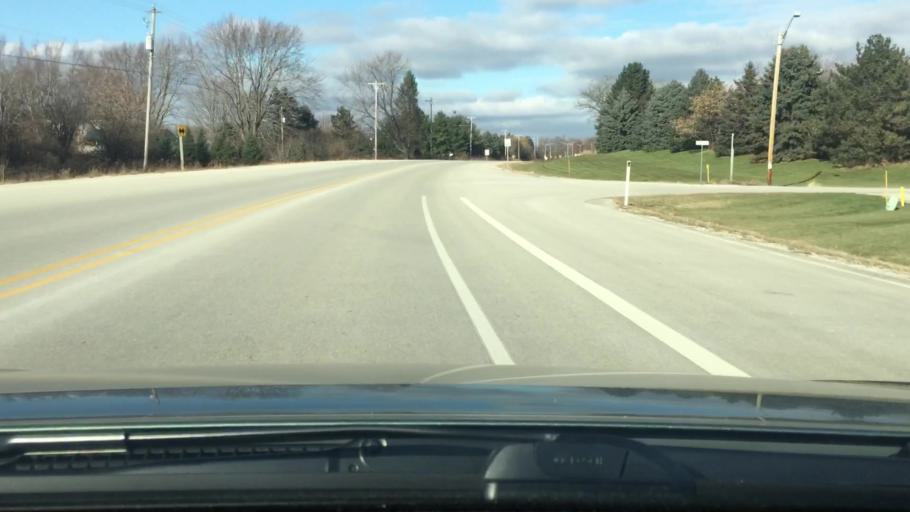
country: US
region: Wisconsin
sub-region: Waukesha County
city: Wales
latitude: 42.9832
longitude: -88.3795
